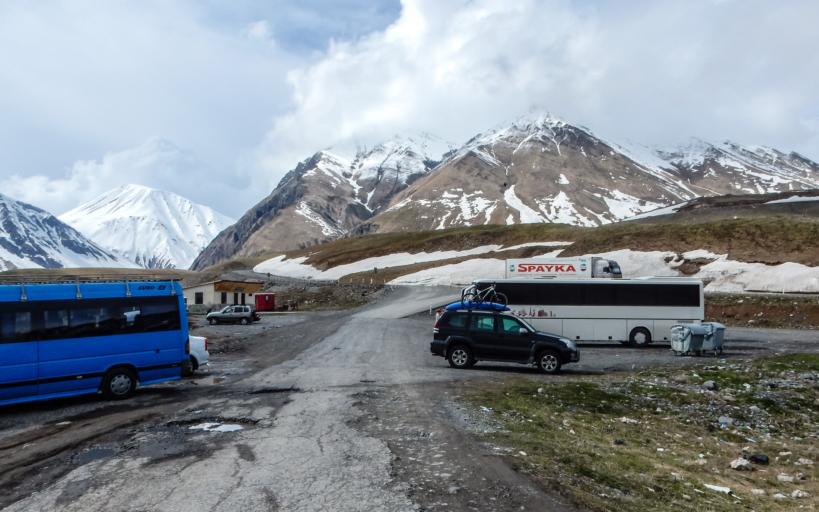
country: GE
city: Gudauri
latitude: 42.4926
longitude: 44.4531
